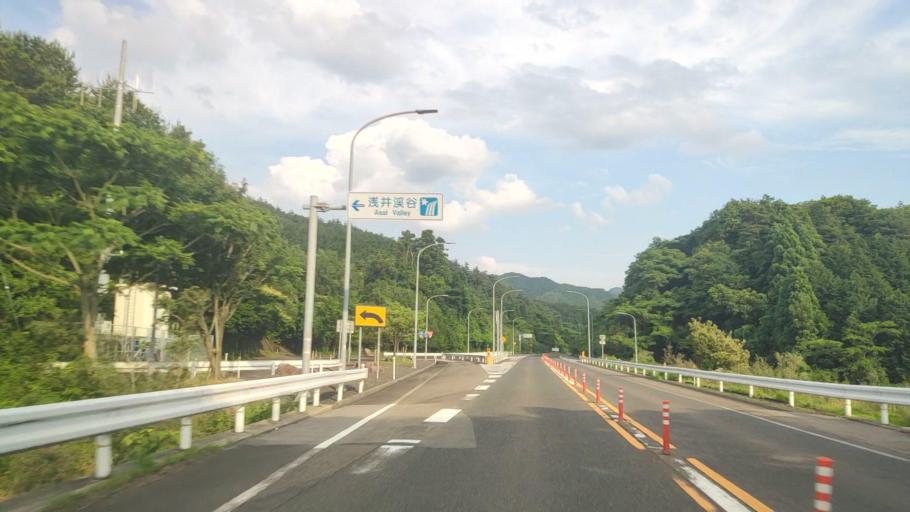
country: JP
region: Tottori
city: Kurayoshi
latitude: 35.3395
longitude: 133.7515
